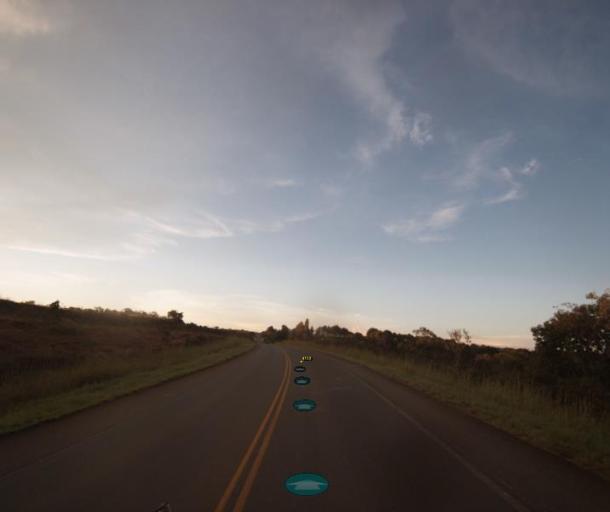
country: BR
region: Goias
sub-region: Abadiania
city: Abadiania
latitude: -16.0801
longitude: -48.8521
